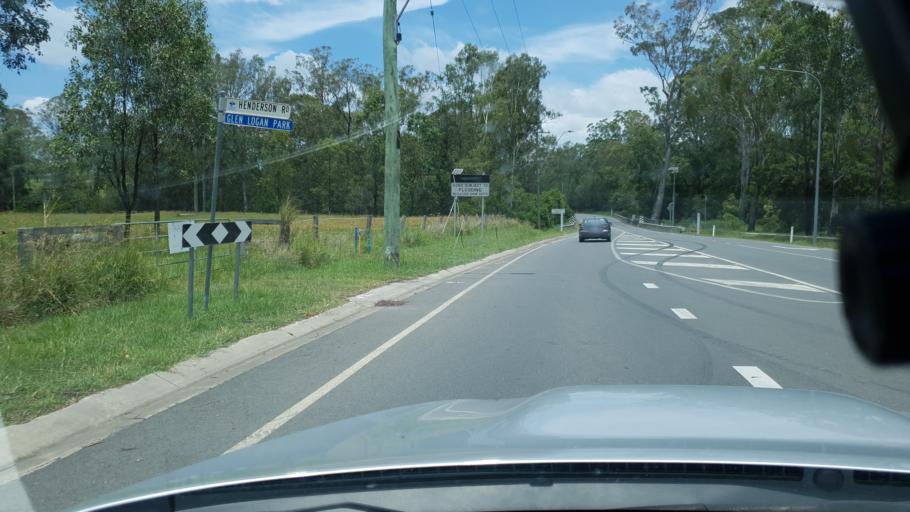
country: AU
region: Queensland
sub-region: Logan
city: North Maclean
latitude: -27.8284
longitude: 153.0146
